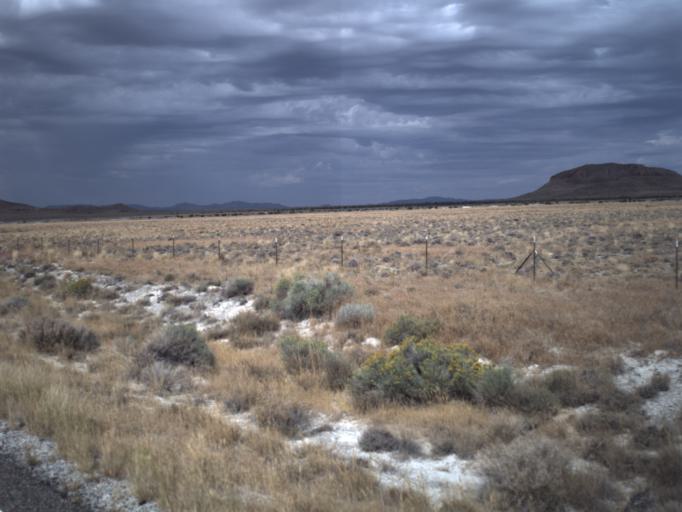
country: US
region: Utah
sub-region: Tooele County
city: Wendover
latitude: 41.4325
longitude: -113.7849
